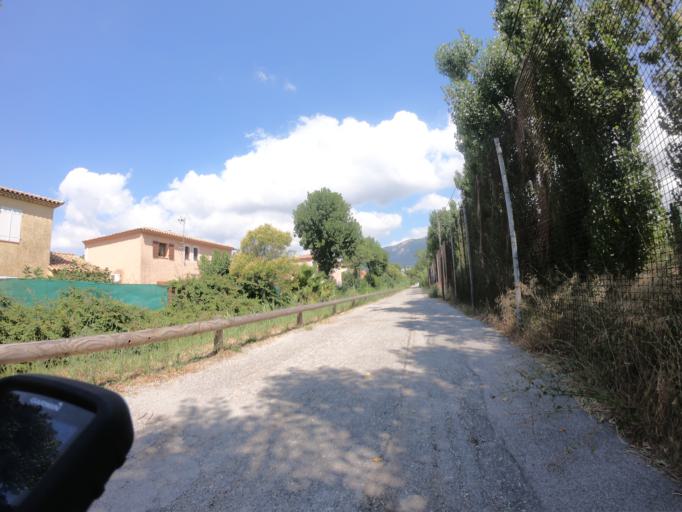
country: FR
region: Provence-Alpes-Cote d'Azur
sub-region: Departement du Var
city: La Garde
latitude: 43.1302
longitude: 6.0264
